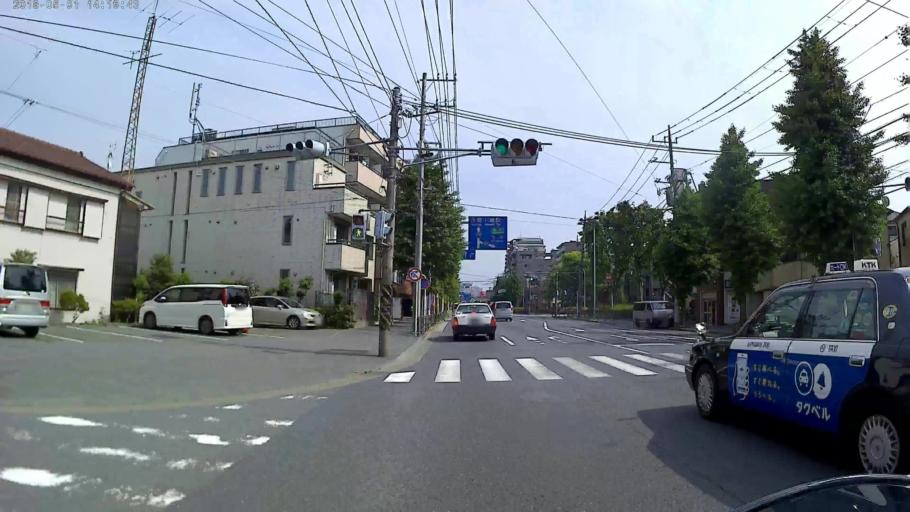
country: JP
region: Kanagawa
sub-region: Kawasaki-shi
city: Kawasaki
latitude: 35.5538
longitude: 139.6793
